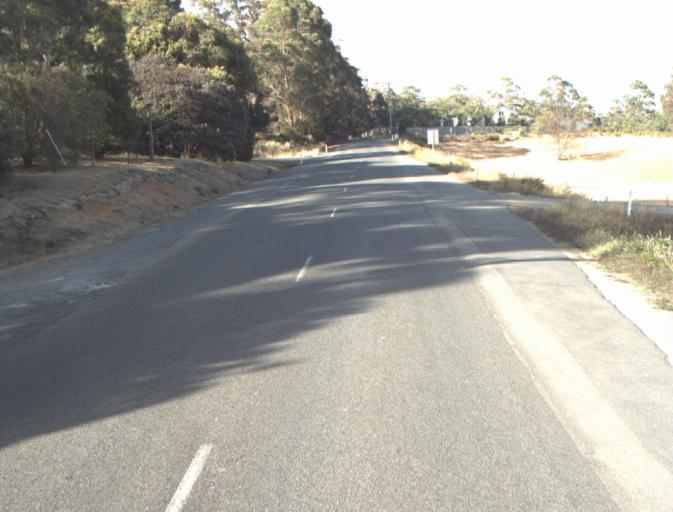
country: AU
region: Tasmania
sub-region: Launceston
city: Mayfield
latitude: -41.2092
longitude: 147.2144
